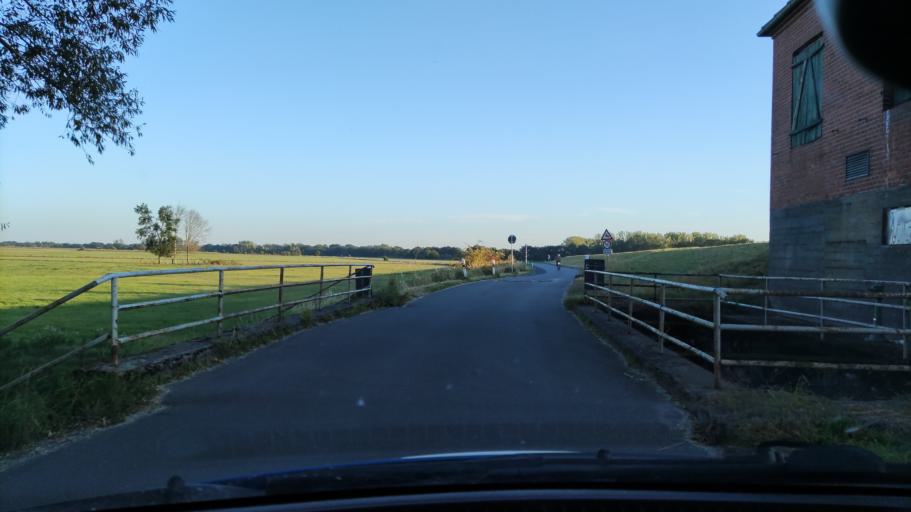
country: DE
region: Lower Saxony
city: Hitzacker
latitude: 53.1256
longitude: 11.0644
